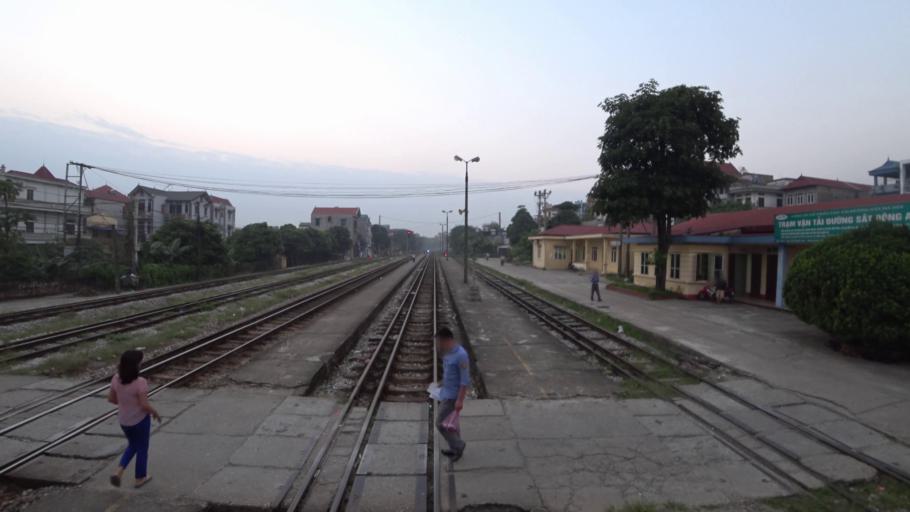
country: VN
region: Ha Noi
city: Soc Son
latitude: 21.2008
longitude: 105.8548
